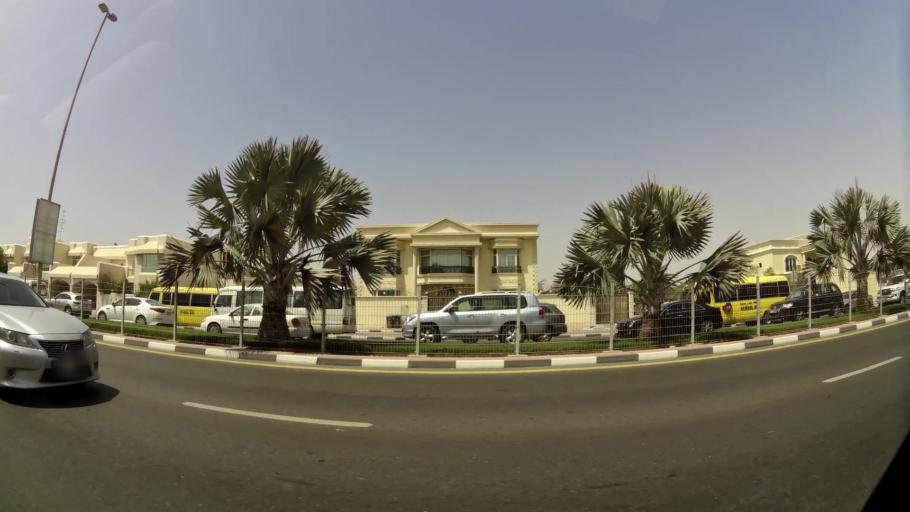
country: AE
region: Dubai
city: Dubai
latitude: 25.1530
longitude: 55.2182
